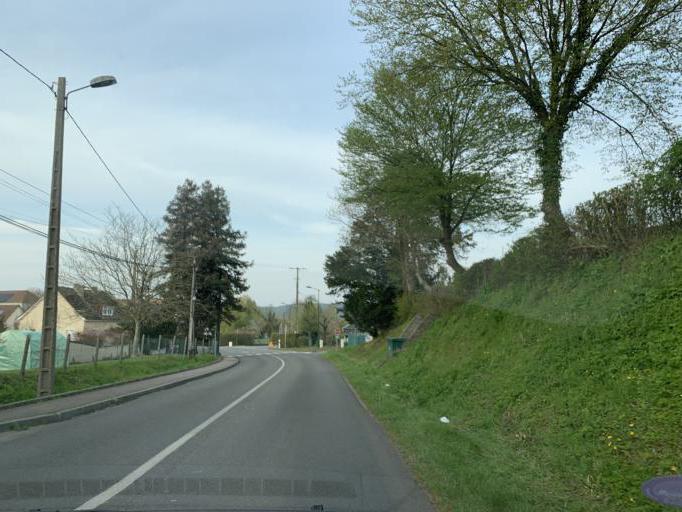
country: FR
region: Haute-Normandie
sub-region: Departement de la Seine-Maritime
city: La Mailleraye-sur-Seine
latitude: 49.4770
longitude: 0.7743
